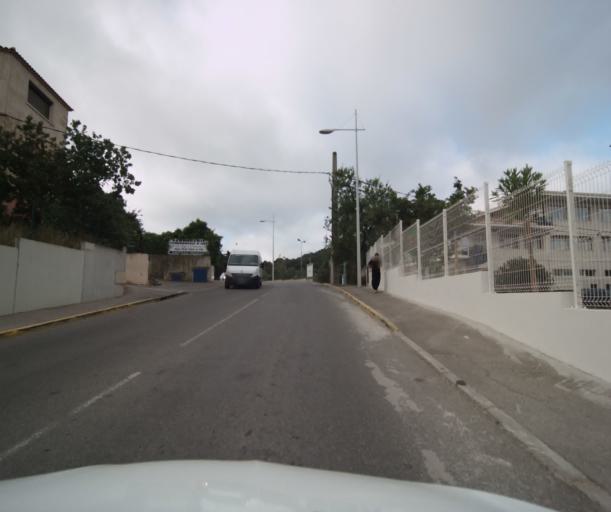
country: FR
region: Provence-Alpes-Cote d'Azur
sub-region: Departement du Var
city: Six-Fours-les-Plages
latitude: 43.1092
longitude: 5.8430
